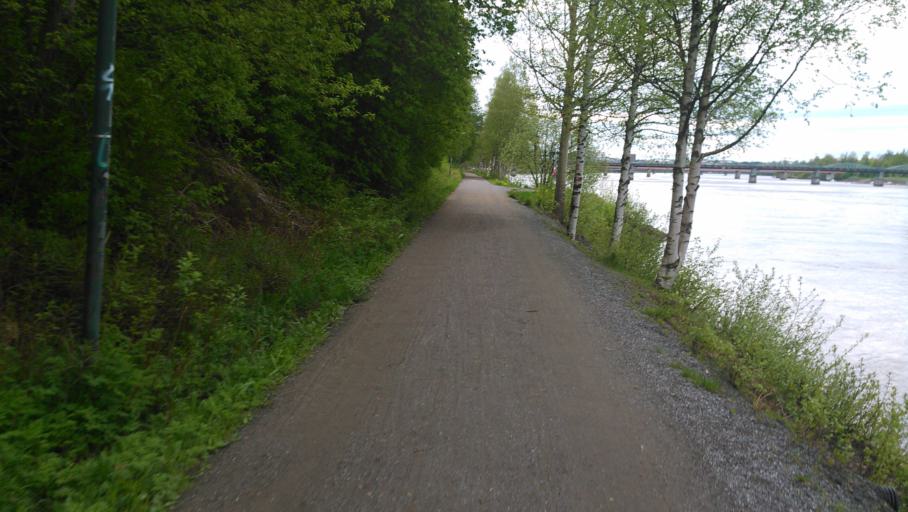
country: SE
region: Vaesterbotten
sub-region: Umea Kommun
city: Umea
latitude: 63.8270
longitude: 20.2412
